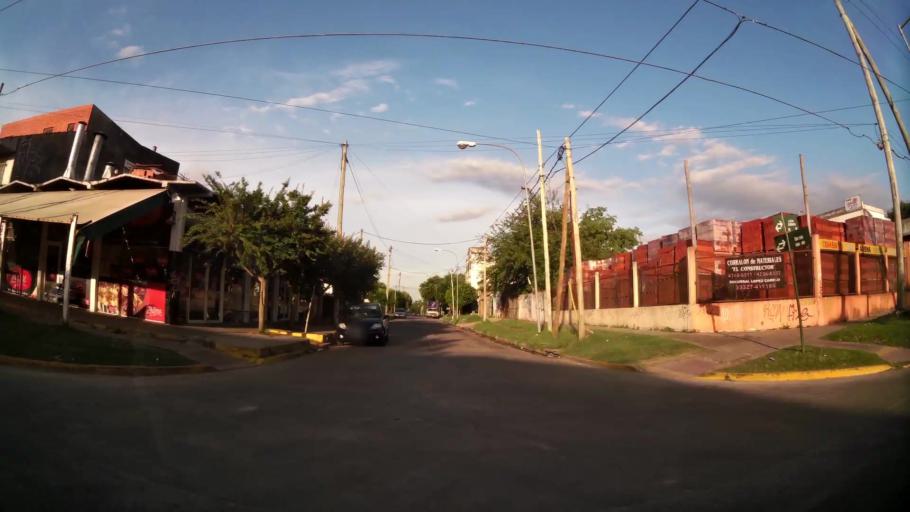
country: AR
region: Buenos Aires
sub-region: Partido de Tigre
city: Tigre
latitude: -34.4556
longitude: -58.6401
